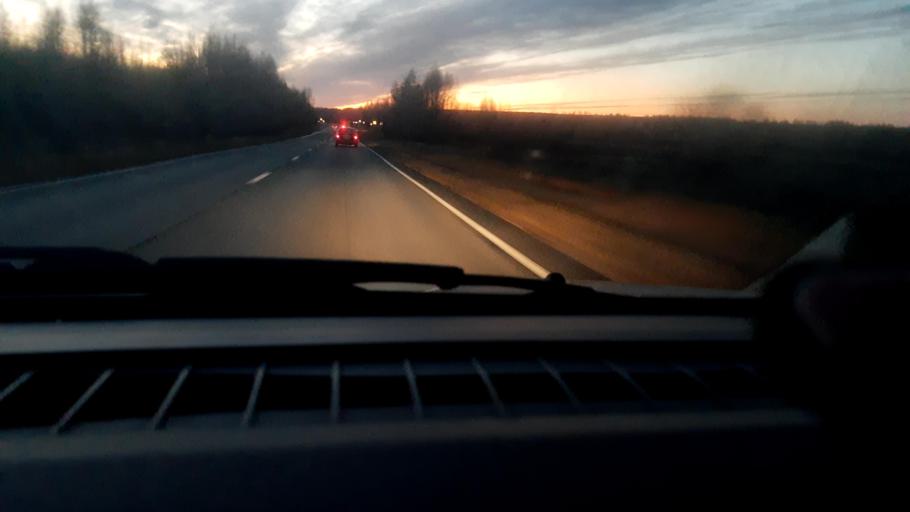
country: RU
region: Nizjnij Novgorod
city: Sukhobezvodnoye
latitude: 56.8605
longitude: 44.8606
